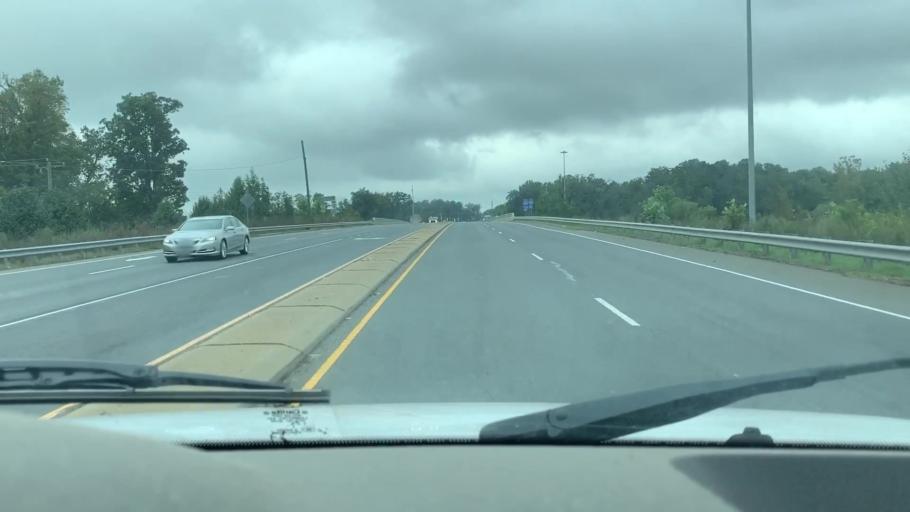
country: US
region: North Carolina
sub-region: Mecklenburg County
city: Huntersville
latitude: 35.3642
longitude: -80.8261
